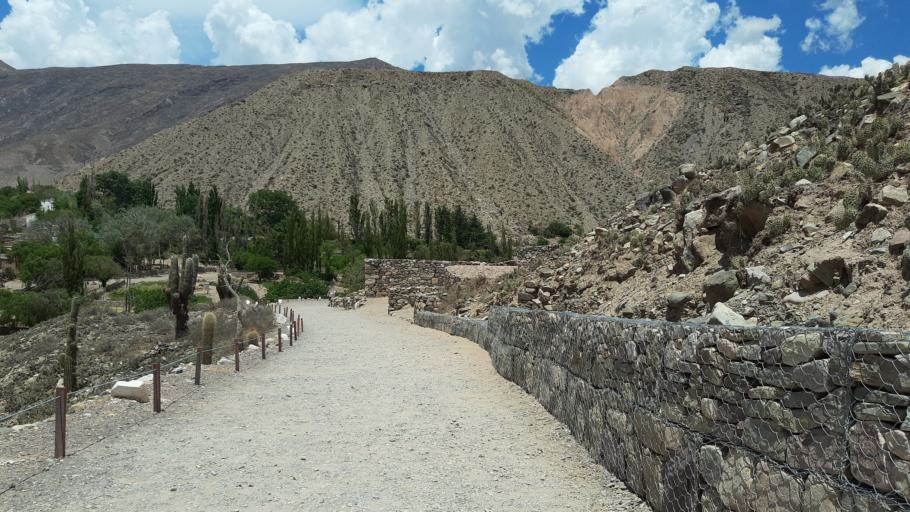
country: AR
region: Jujuy
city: Maimara
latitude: -23.5849
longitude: -65.4011
